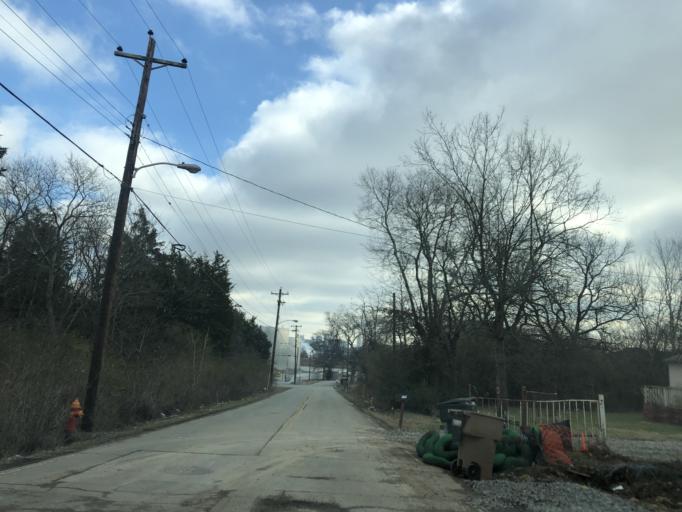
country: US
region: Tennessee
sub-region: Davidson County
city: Nashville
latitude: 36.2054
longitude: -86.8105
